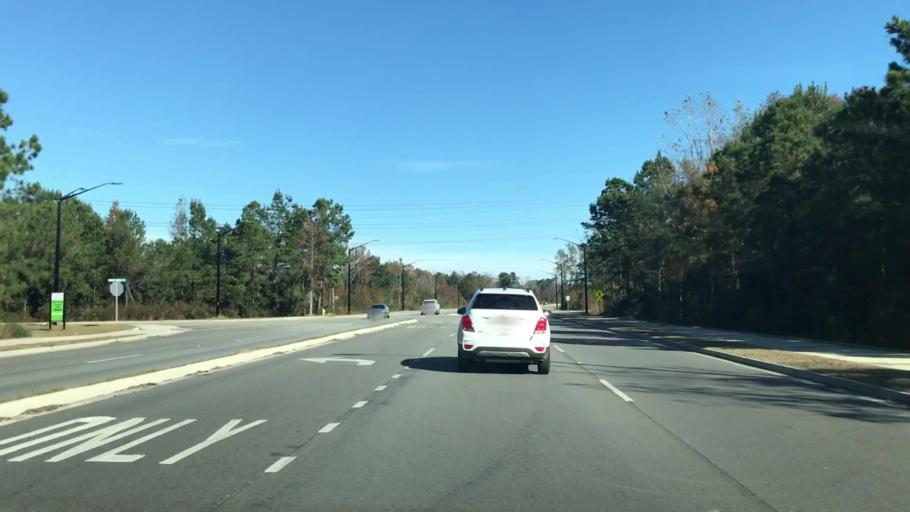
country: US
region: South Carolina
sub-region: Dorchester County
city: Summerville
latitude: 33.0421
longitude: -80.1820
